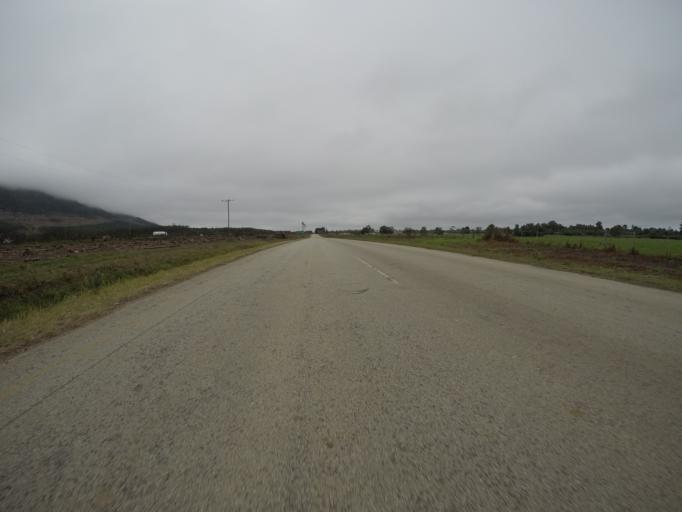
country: ZA
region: Eastern Cape
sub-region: Cacadu District Municipality
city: Kareedouw
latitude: -33.9857
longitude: 24.0662
